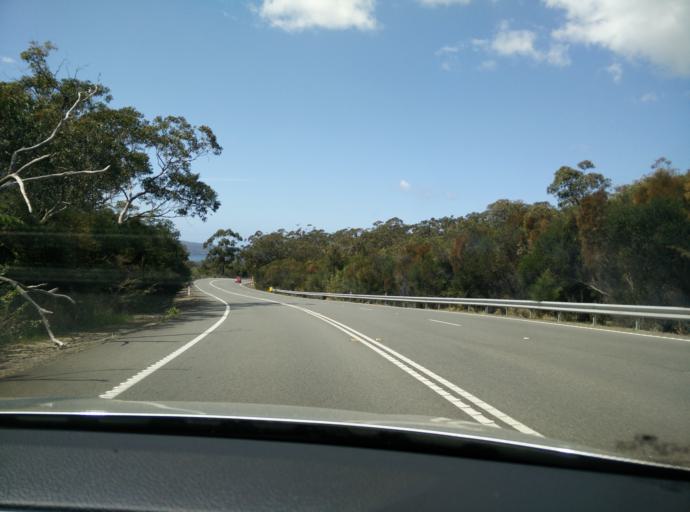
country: AU
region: New South Wales
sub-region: Gosford Shire
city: Blackwall
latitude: -33.4759
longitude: 151.2891
